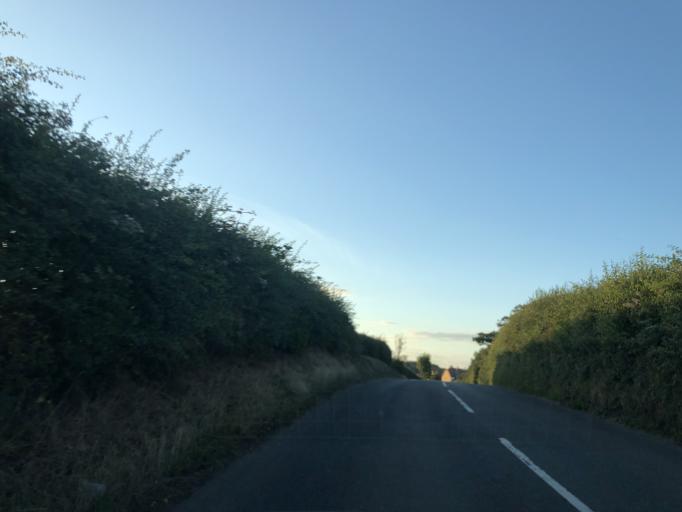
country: GB
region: England
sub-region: Isle of Wight
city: Niton
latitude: 50.6428
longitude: -1.2789
